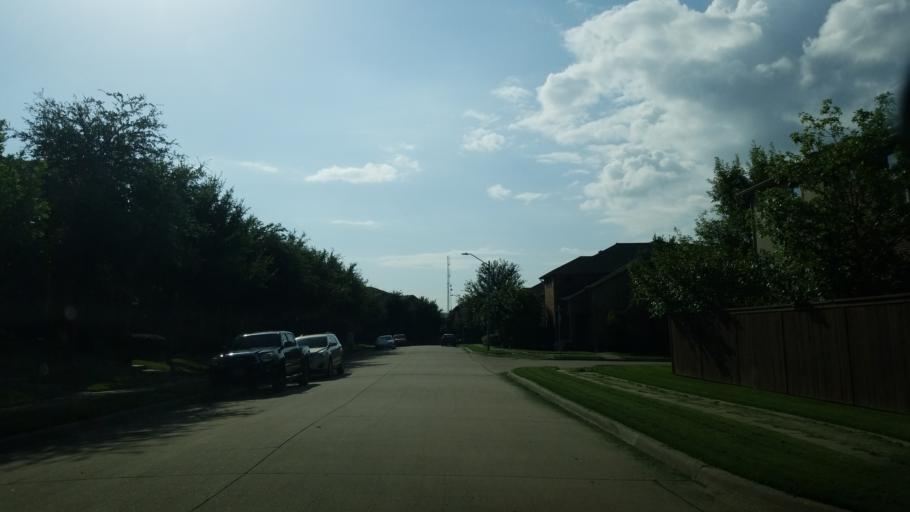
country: US
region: Texas
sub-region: Dallas County
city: Coppell
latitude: 32.9224
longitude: -96.9699
